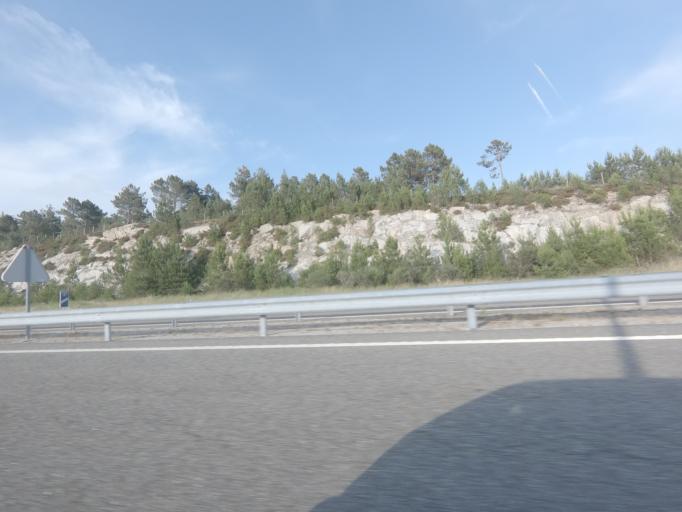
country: PT
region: Vila Real
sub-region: Vila Pouca de Aguiar
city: Vila Pouca de Aguiar
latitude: 41.5022
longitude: -7.6562
